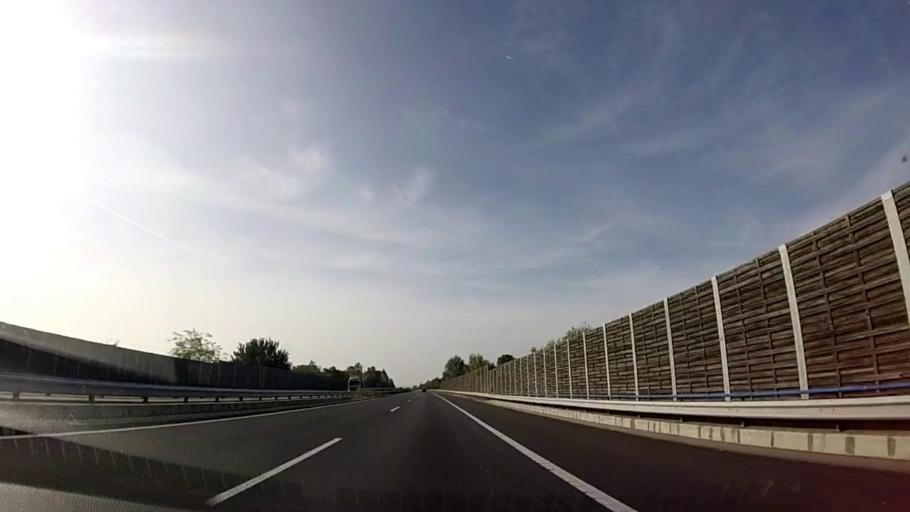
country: HU
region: Somogy
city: Balatonszabadi
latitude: 46.9641
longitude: 18.1617
